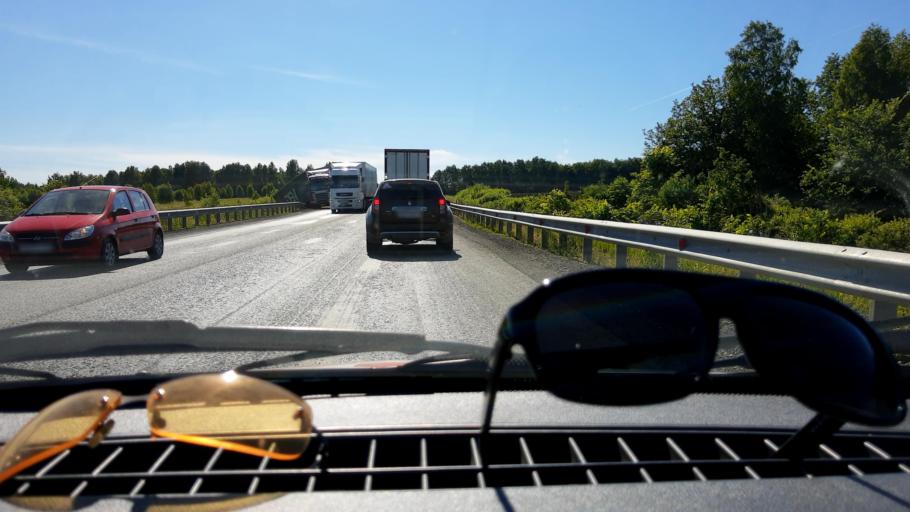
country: RU
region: Bashkortostan
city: Kudeyevskiy
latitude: 54.8153
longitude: 56.6933
